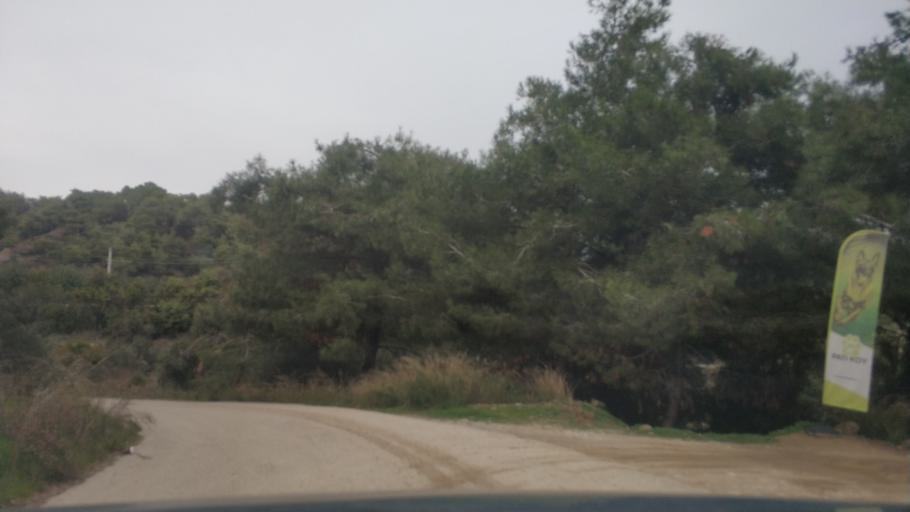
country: TR
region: Adana
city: Adana
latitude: 37.0984
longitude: 35.2895
